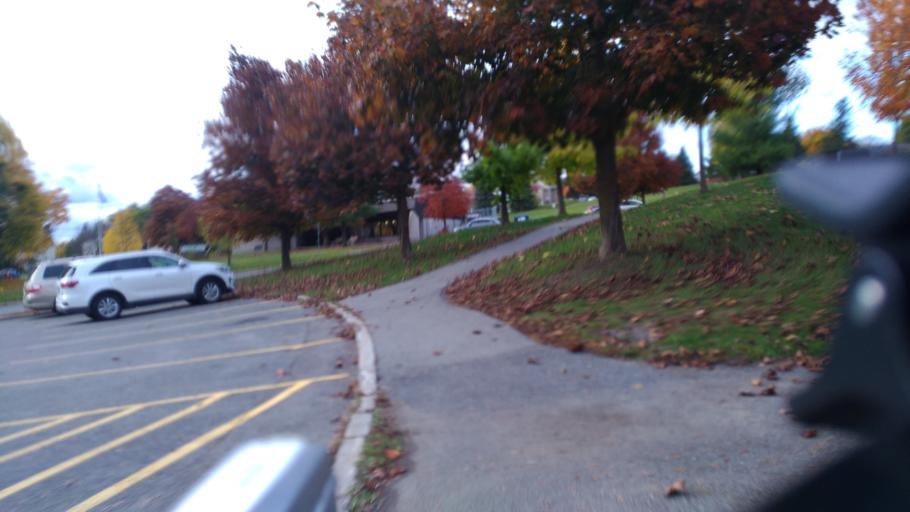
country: CA
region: Ontario
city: Bells Corners
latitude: 45.2952
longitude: -75.8850
